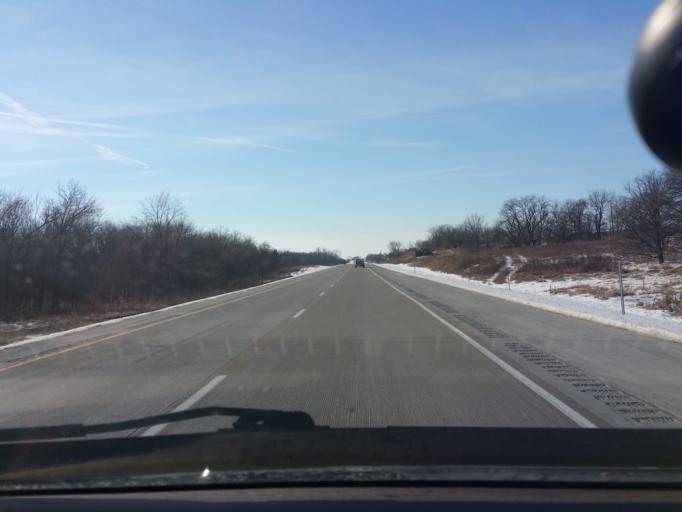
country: US
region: Iowa
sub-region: Decatur County
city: Lamoni
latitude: 40.6044
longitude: -93.9093
